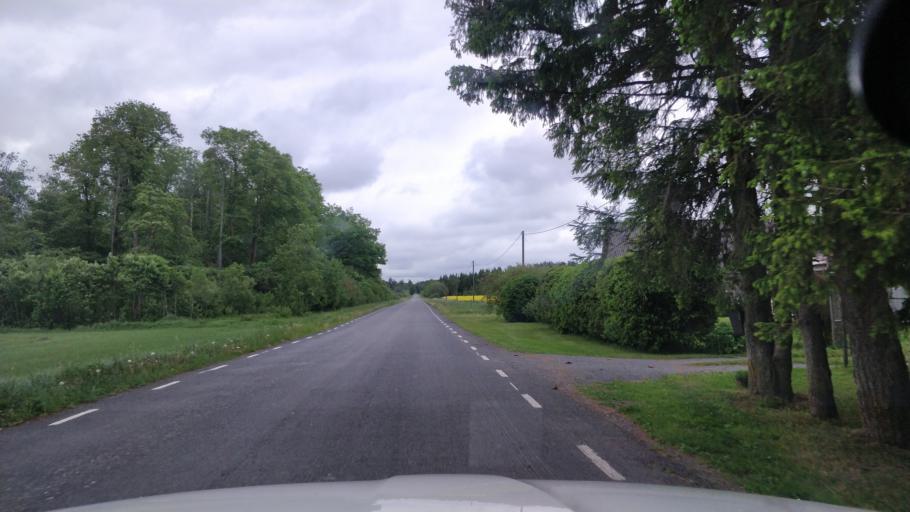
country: EE
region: Raplamaa
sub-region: Maerjamaa vald
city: Marjamaa
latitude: 58.7560
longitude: 24.2375
